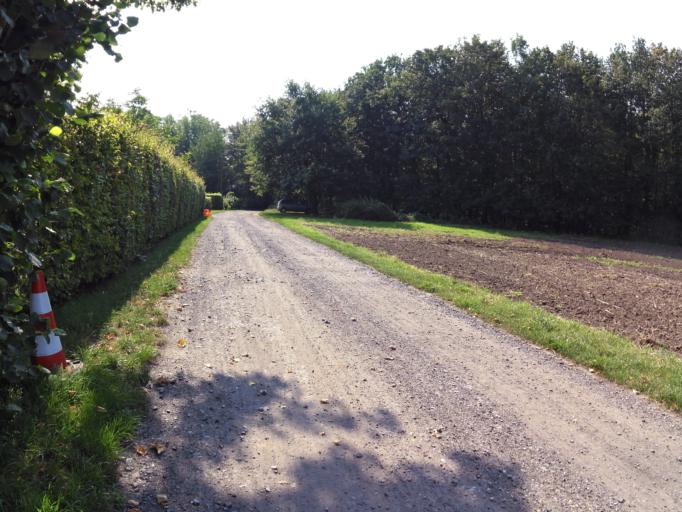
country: DE
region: North Rhine-Westphalia
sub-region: Regierungsbezirk Munster
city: Altenberge
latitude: 51.9745
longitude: 7.4981
